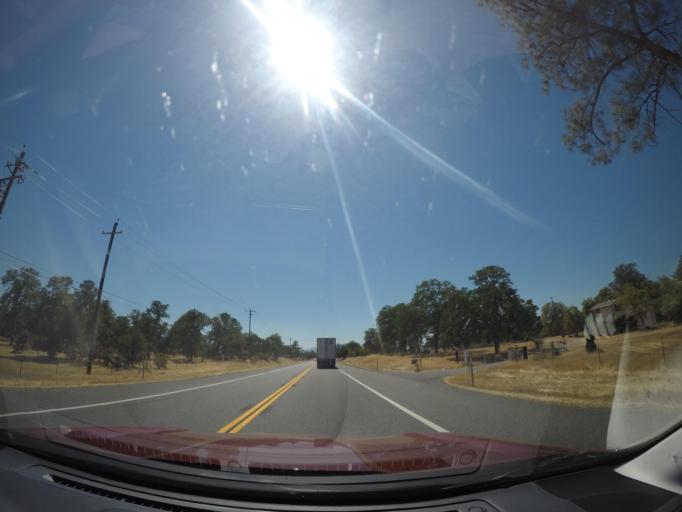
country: US
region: California
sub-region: Shasta County
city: Bella Vista
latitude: 40.6339
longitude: -122.2575
